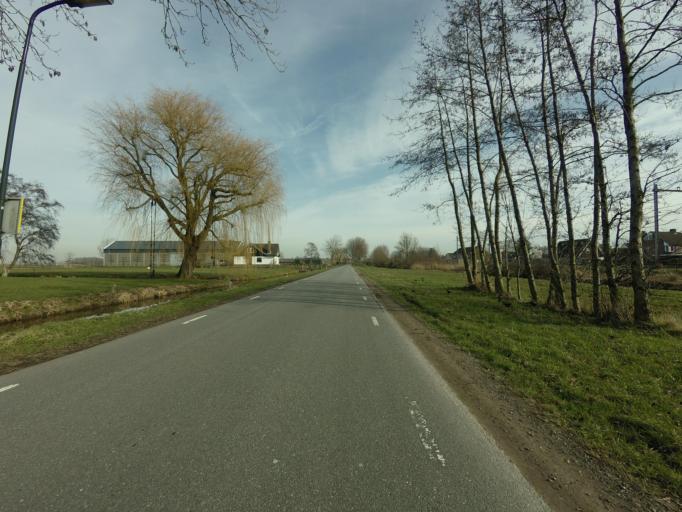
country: NL
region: South Holland
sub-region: Gemeente Hardinxveld-Giessendam
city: Neder-Hardinxveld
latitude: 51.8305
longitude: 4.8285
